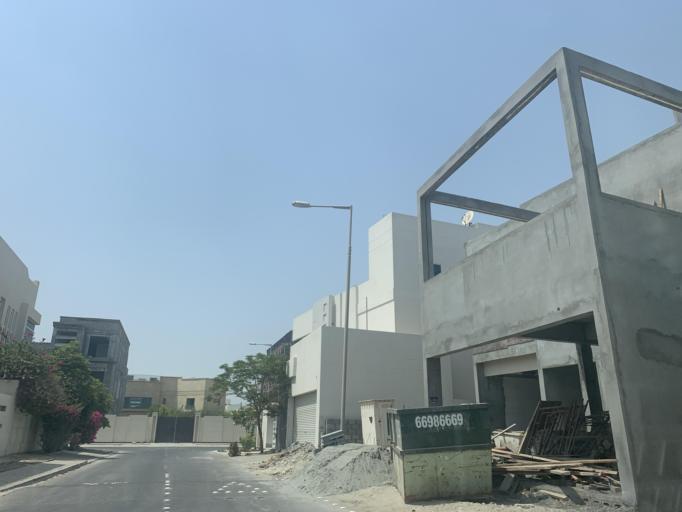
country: BH
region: Northern
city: Madinat `Isa
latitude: 26.1954
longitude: 50.4931
